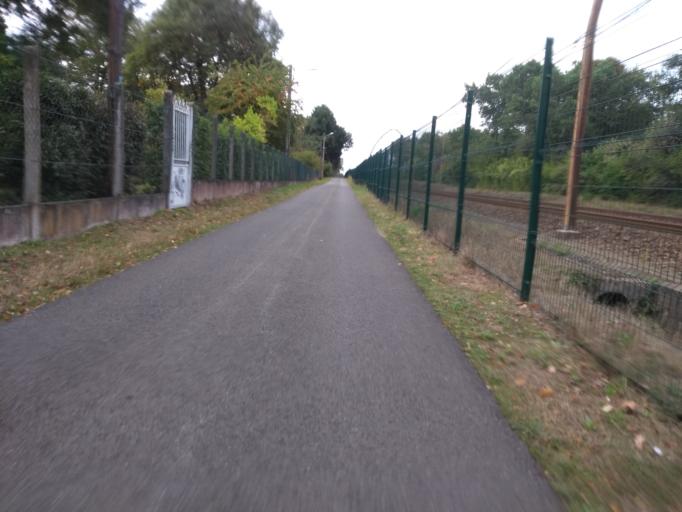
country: FR
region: Aquitaine
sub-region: Departement de la Gironde
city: Cestas
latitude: 44.7844
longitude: -0.6763
